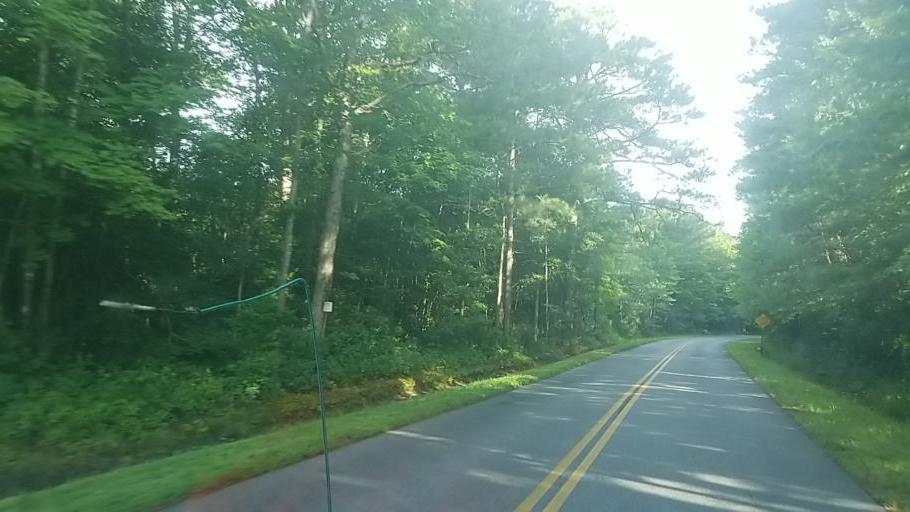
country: US
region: Maryland
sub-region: Worcester County
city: West Ocean City
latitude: 38.3187
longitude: -75.1463
